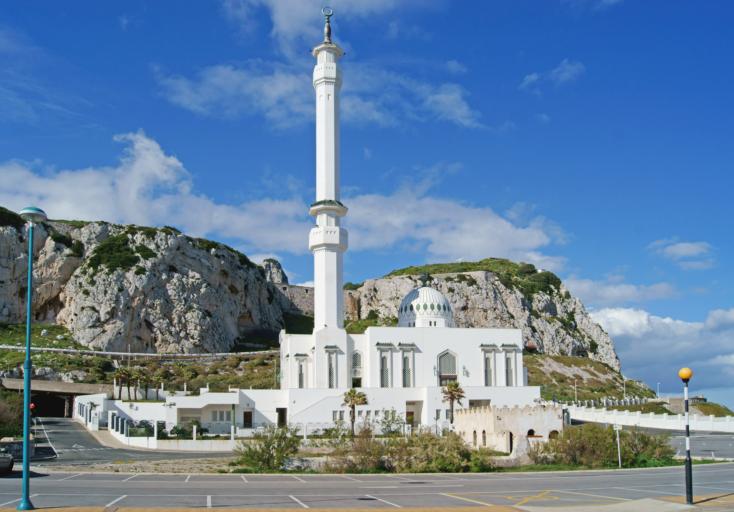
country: GI
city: Gibraltar
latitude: 36.1117
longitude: -5.3457
